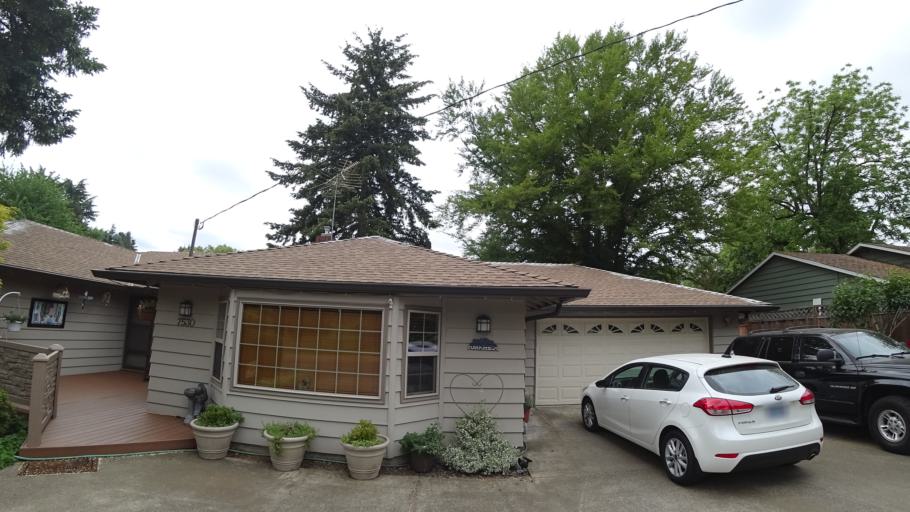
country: US
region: Oregon
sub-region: Washington County
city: Garden Home-Whitford
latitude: 45.4639
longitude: -122.7544
